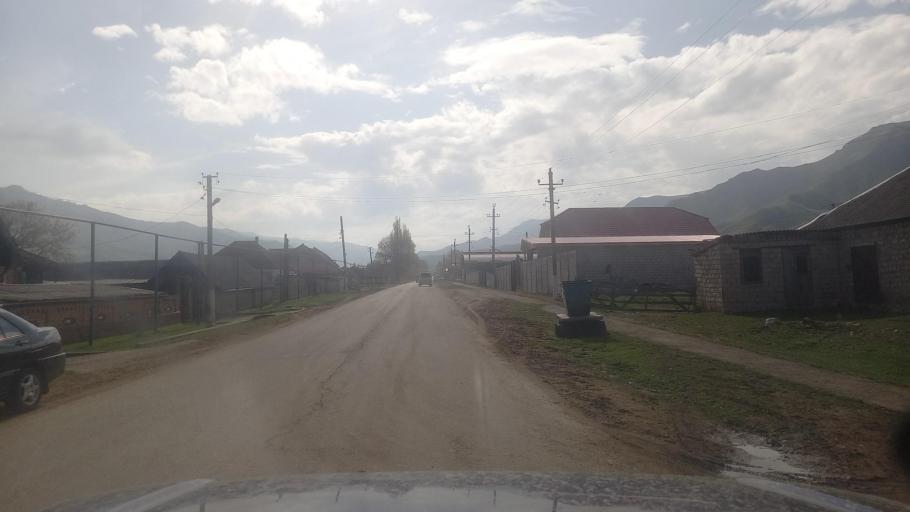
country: RU
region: Kabardino-Balkariya
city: Kamennomostskoye
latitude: 43.7315
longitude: 42.9514
